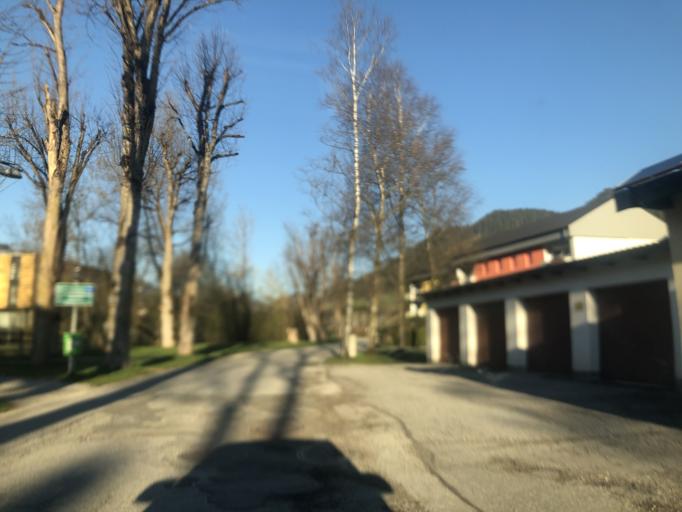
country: AT
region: Styria
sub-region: Politischer Bezirk Liezen
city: Schladming
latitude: 47.3928
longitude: 13.6782
